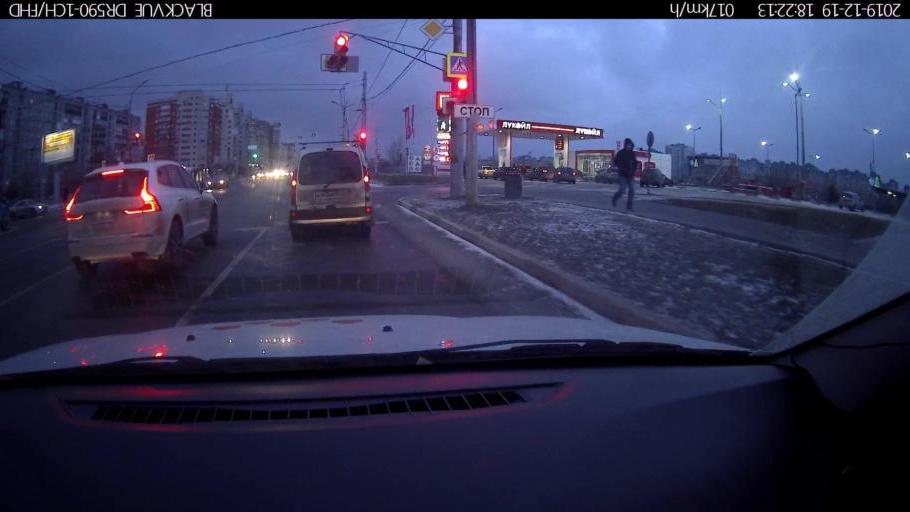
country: RU
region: Nizjnij Novgorod
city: Nizhniy Novgorod
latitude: 56.3330
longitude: 43.9490
